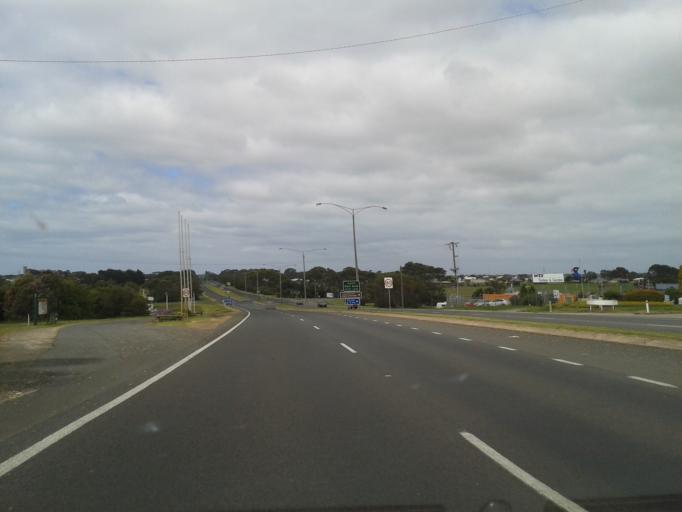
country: AU
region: Victoria
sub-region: Glenelg
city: Portland
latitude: -38.3211
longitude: 141.5969
